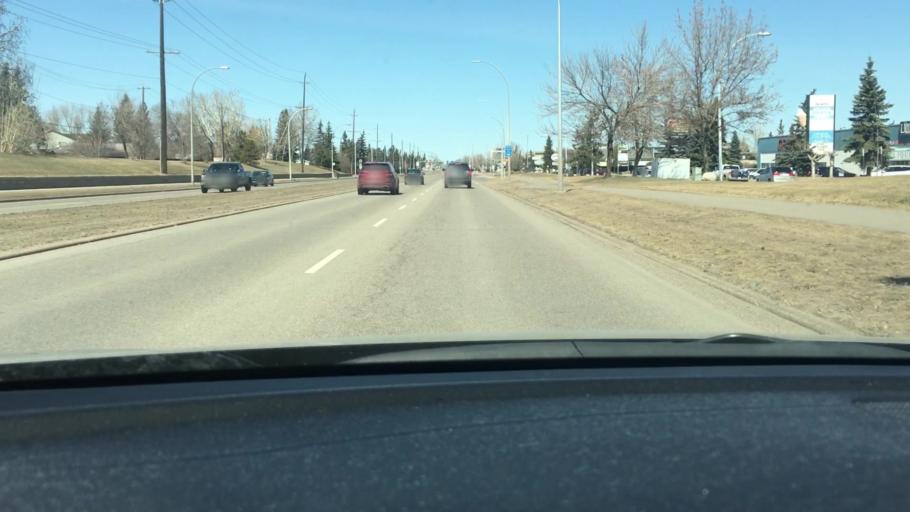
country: CA
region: Alberta
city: Edmonton
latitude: 53.5286
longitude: -113.4185
